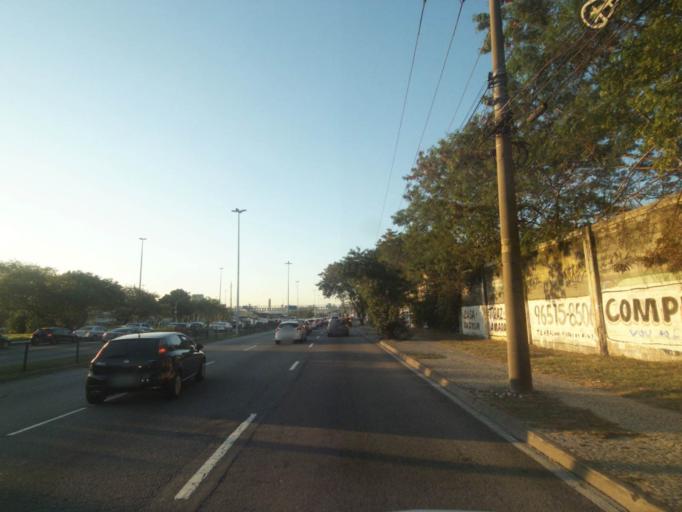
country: BR
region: Rio de Janeiro
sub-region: Rio De Janeiro
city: Rio de Janeiro
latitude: -22.9860
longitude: -43.3654
